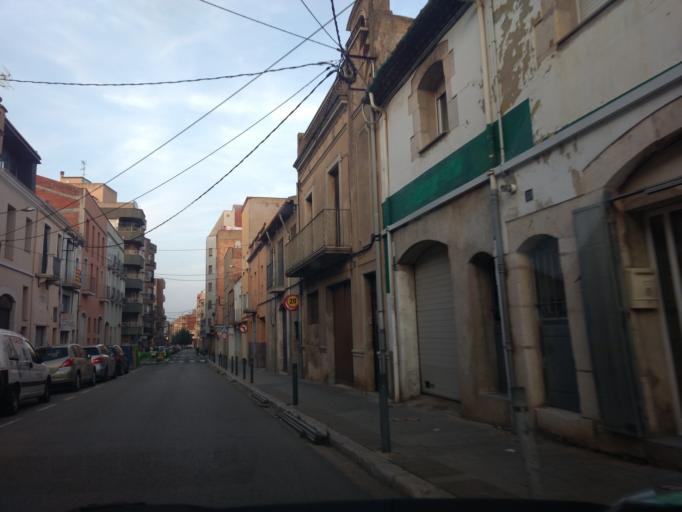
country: ES
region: Catalonia
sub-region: Provincia de Girona
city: Figueres
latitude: 42.2704
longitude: 2.9647
